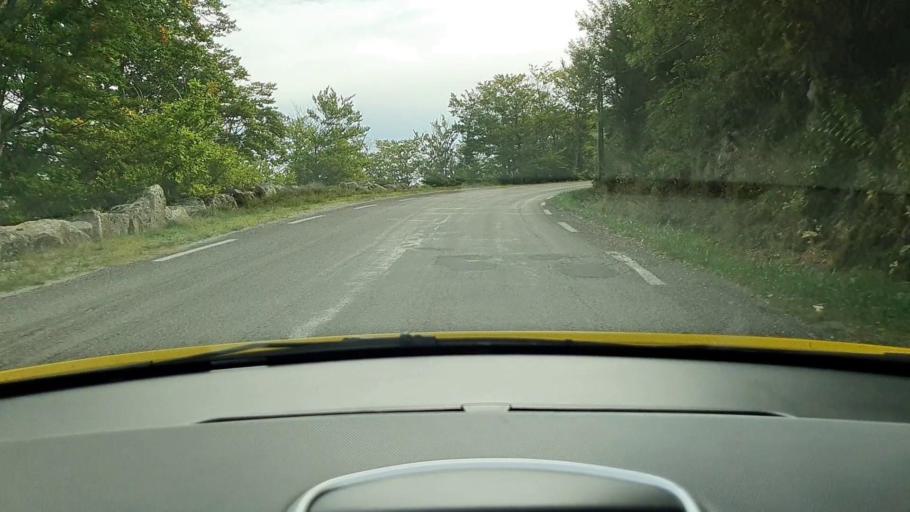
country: FR
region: Languedoc-Roussillon
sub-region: Departement du Gard
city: Le Vigan
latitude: 44.0325
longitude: 3.5792
